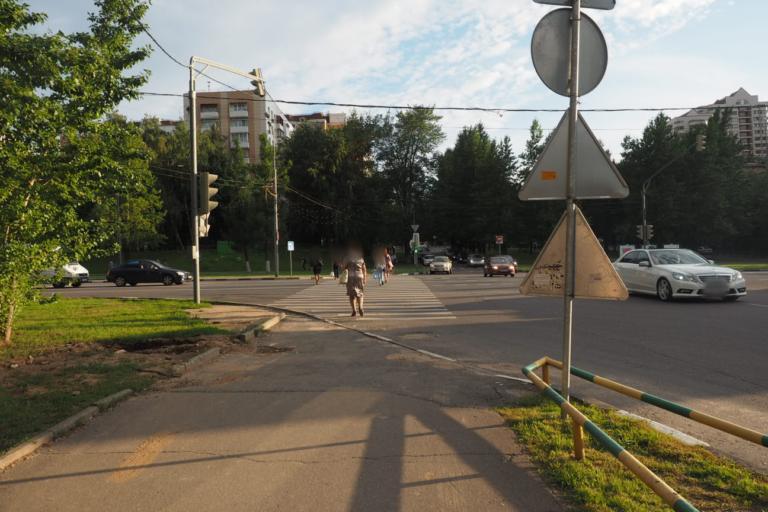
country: RU
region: Moskovskaya
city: Cheremushki
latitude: 55.6750
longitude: 37.5724
